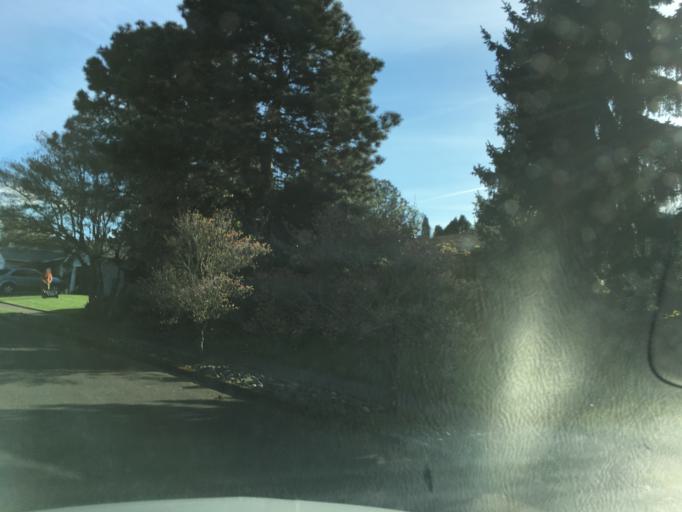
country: US
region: Oregon
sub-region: Multnomah County
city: Lents
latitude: 45.5495
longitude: -122.5199
